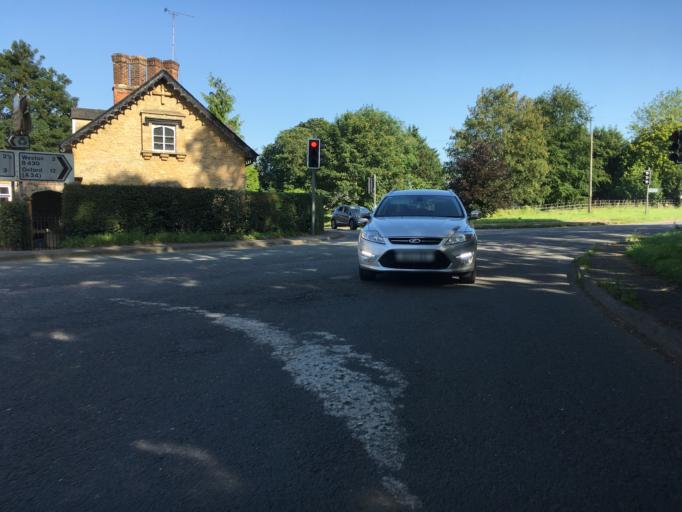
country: GB
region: England
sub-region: Oxfordshire
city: Somerton
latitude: 51.9075
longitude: -1.2250
